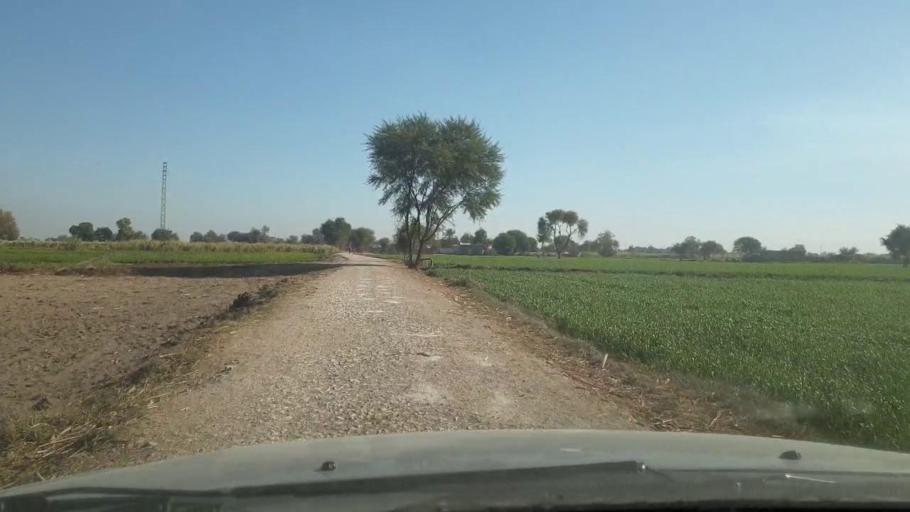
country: PK
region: Sindh
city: Ghotki
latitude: 27.9743
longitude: 69.1893
